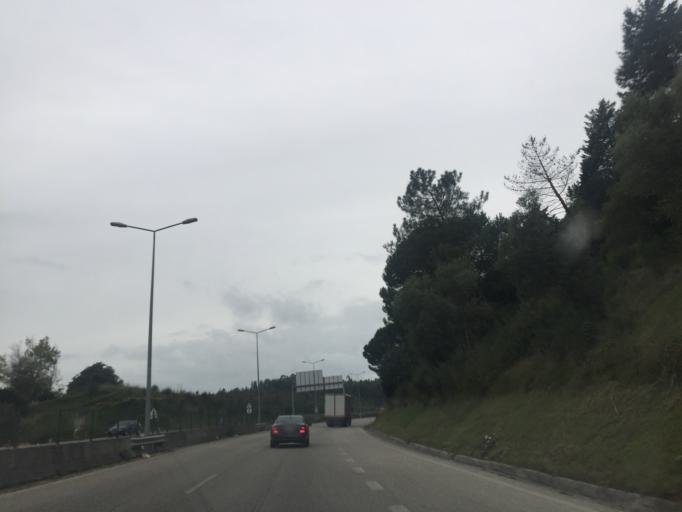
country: PT
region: Coimbra
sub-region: Coimbra
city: Coimbra
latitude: 40.1849
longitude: -8.4317
